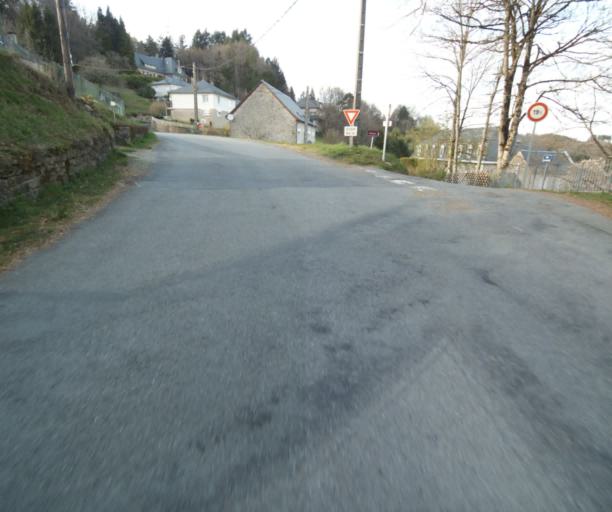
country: FR
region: Limousin
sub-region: Departement de la Correze
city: Correze
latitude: 45.3704
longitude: 1.8711
